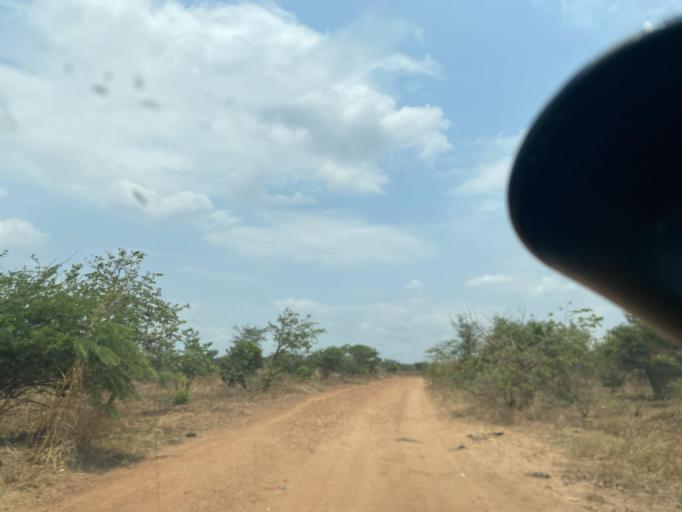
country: ZM
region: Lusaka
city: Chongwe
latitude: -15.5272
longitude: 28.8243
